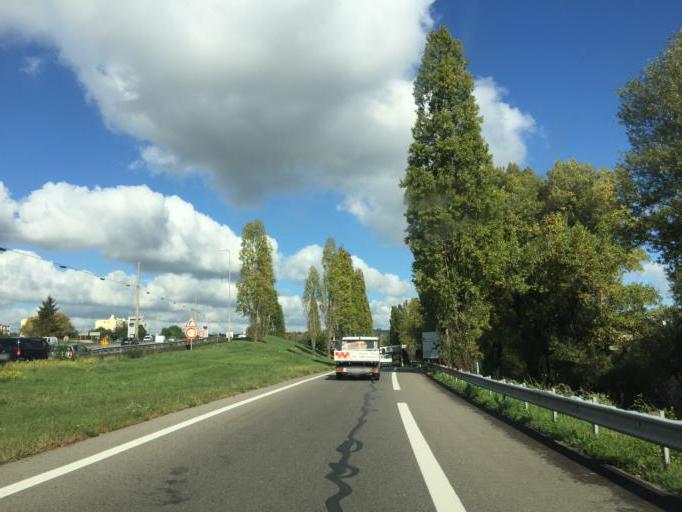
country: FR
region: Rhone-Alpes
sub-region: Departement du Rhone
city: Villeurbanne
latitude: 45.7813
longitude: 4.8939
